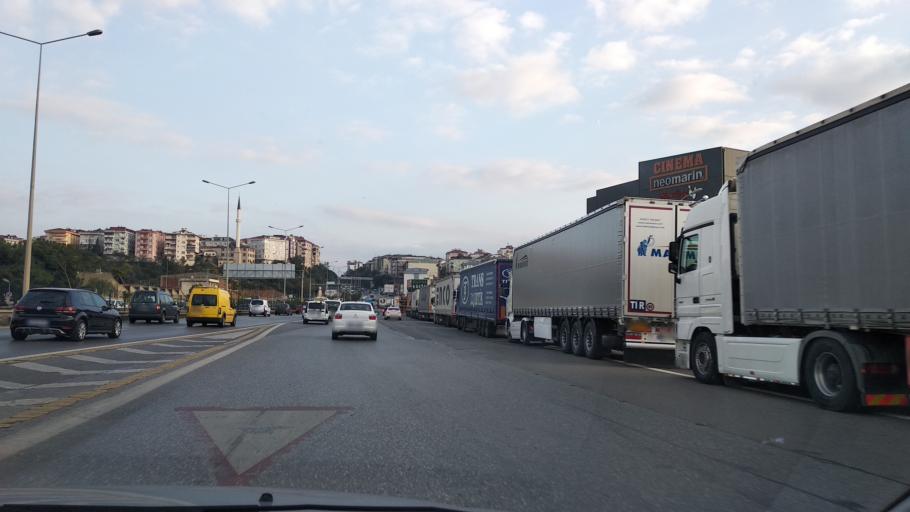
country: TR
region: Istanbul
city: Pendik
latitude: 40.8652
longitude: 29.2741
